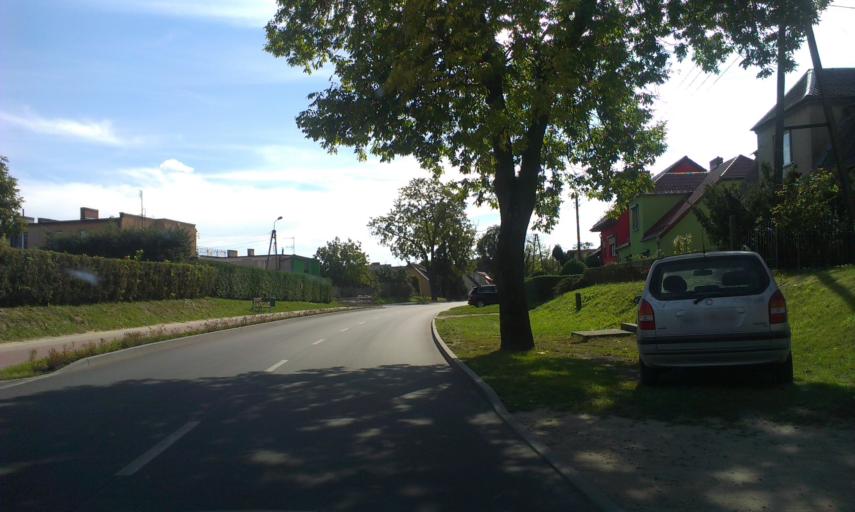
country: PL
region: Greater Poland Voivodeship
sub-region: Powiat pilski
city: Lobzenica
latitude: 53.2669
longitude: 17.2574
